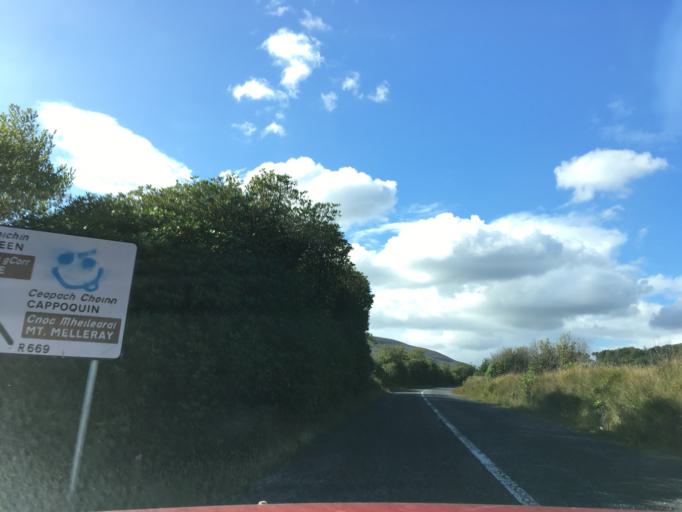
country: IE
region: Munster
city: Cahir
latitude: 52.2187
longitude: -7.9403
